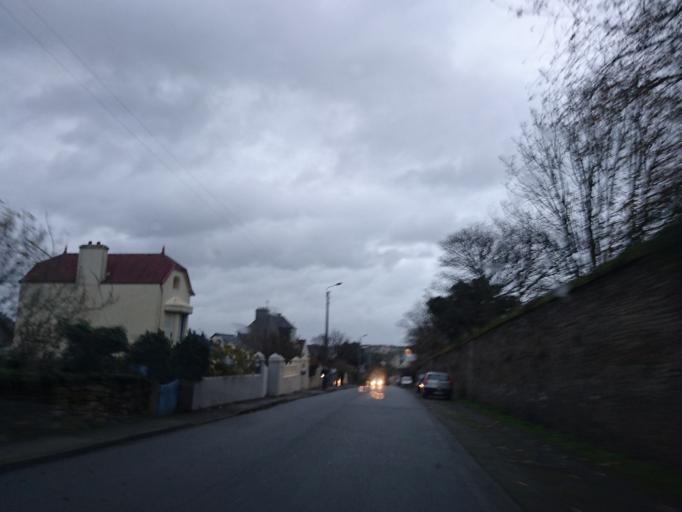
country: FR
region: Brittany
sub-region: Departement du Finistere
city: Le Conquet
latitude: 48.3603
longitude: -4.7671
